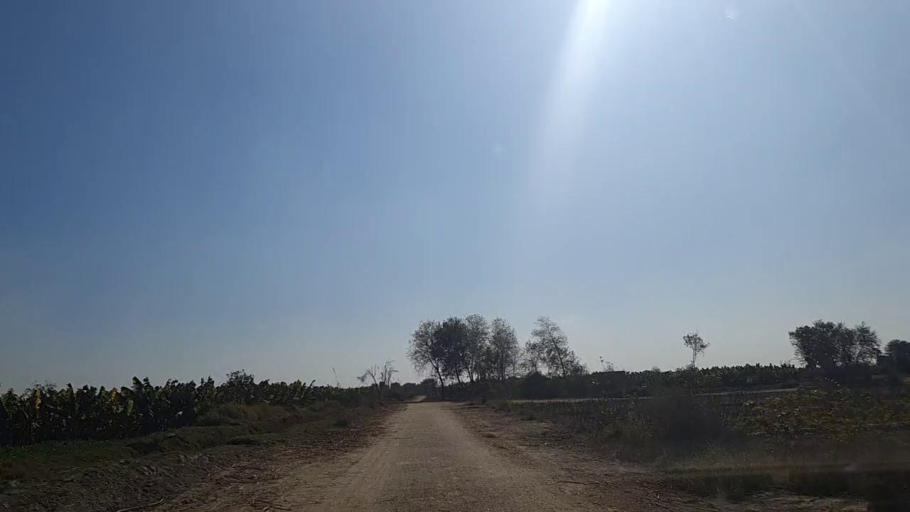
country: PK
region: Sindh
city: Sakrand
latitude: 26.2397
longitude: 68.1998
